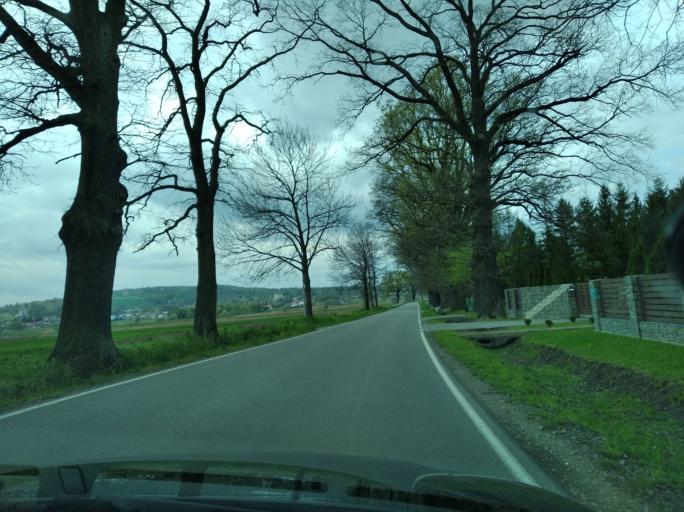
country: PL
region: Subcarpathian Voivodeship
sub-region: Powiat brzozowski
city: Turze Pole
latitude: 49.6473
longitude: 21.9945
